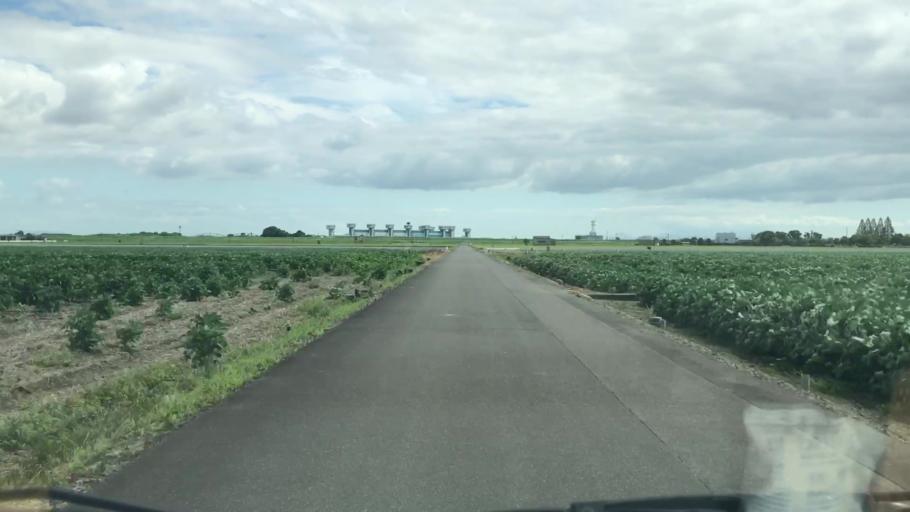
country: JP
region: Saga Prefecture
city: Saga-shi
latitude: 33.2124
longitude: 130.1839
